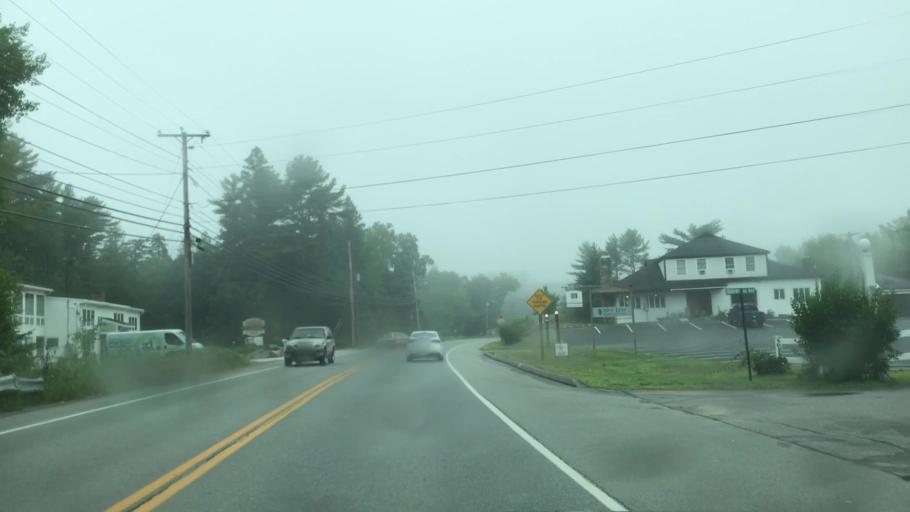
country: US
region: Maine
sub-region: Knox County
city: Rockport
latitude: 44.1976
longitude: -69.0798
